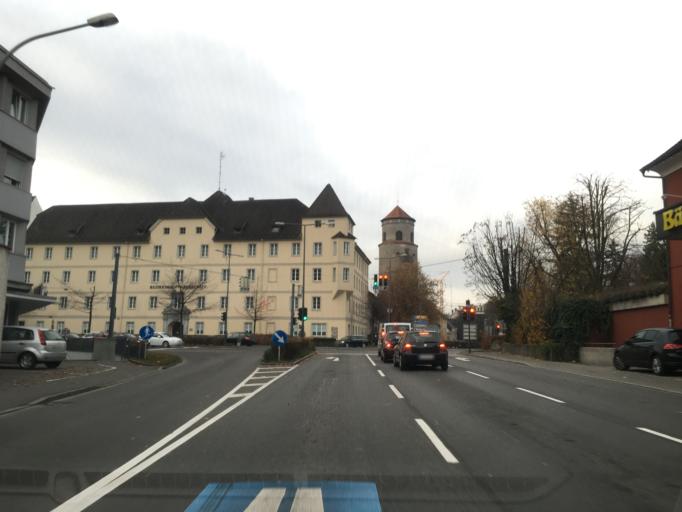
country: AT
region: Vorarlberg
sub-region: Politischer Bezirk Feldkirch
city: Feldkirch
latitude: 47.2393
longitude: 9.5986
